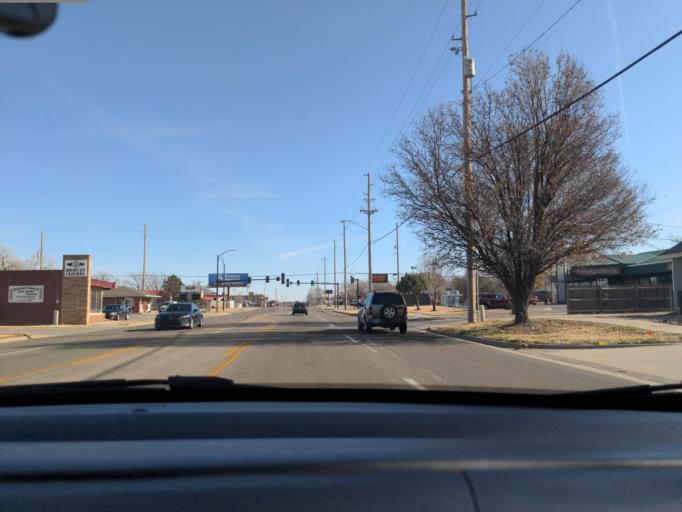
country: US
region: Kansas
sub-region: Sedgwick County
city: Wichita
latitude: 37.6948
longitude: -97.3817
